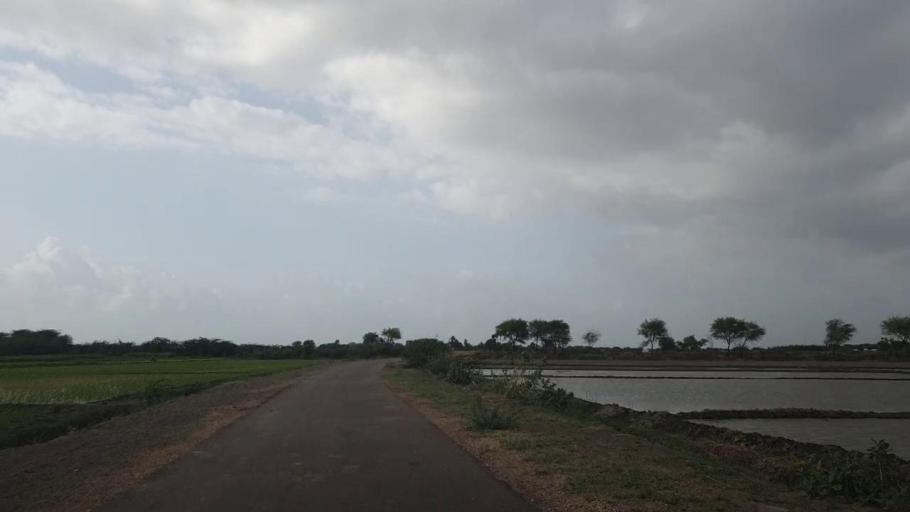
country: PK
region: Sindh
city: Kadhan
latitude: 24.6026
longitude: 69.0554
